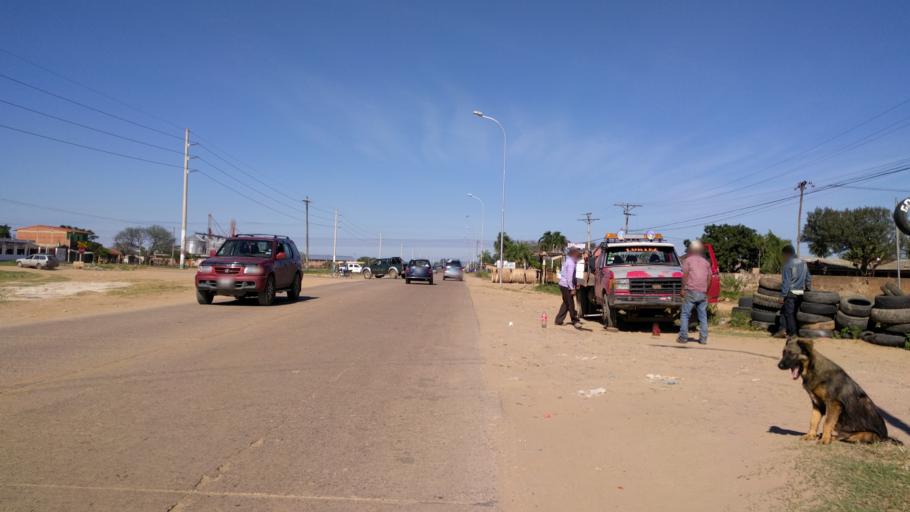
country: BO
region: Santa Cruz
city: Santa Cruz de la Sierra
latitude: -17.8653
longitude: -63.1894
